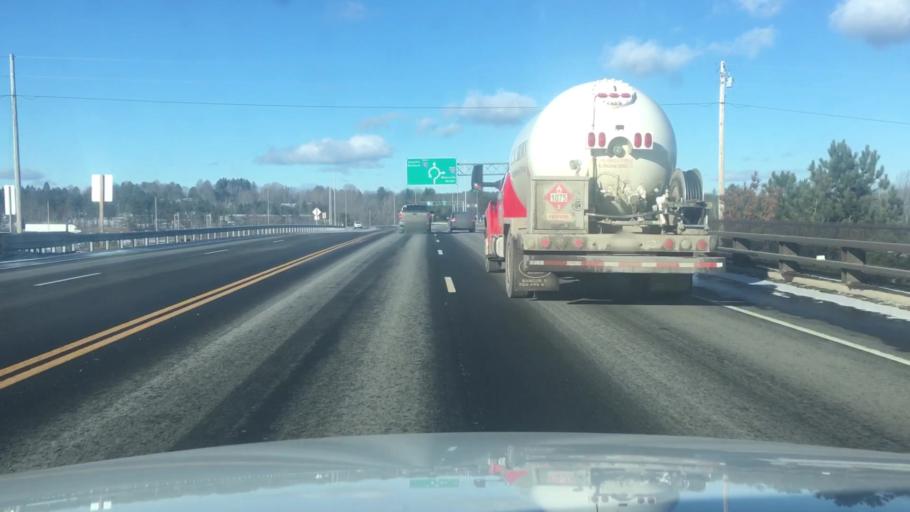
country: US
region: Maine
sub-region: Kennebec County
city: Augusta
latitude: 44.3517
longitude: -69.7780
